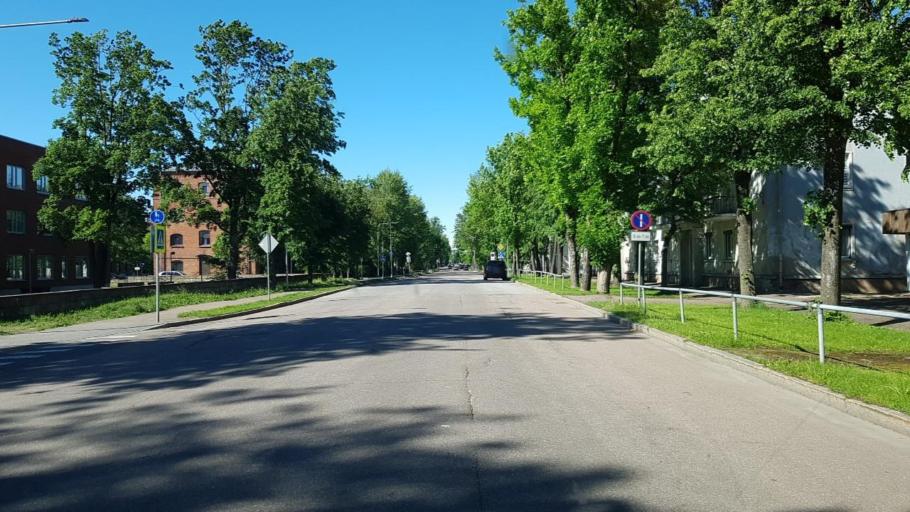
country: EE
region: Ida-Virumaa
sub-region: Narva linn
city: Narva
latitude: 59.3618
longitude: 28.1953
